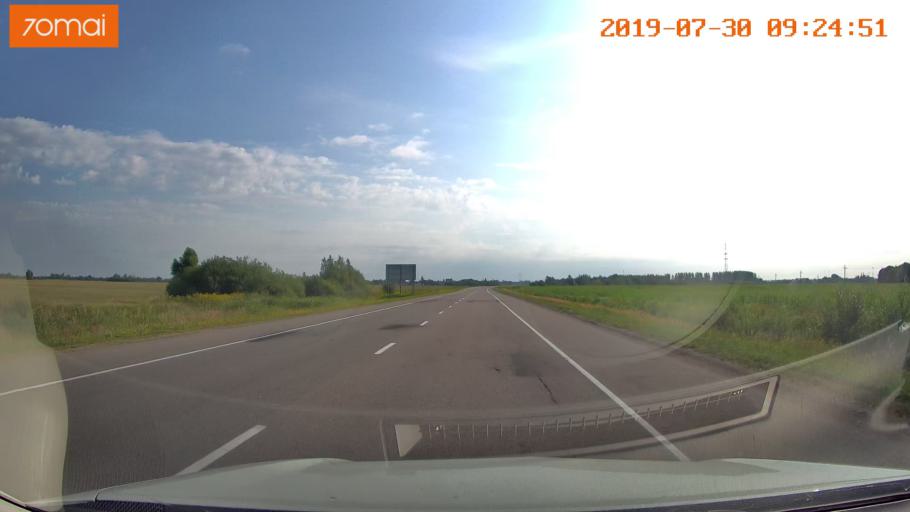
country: LT
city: Kybartai
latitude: 54.6353
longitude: 22.7030
